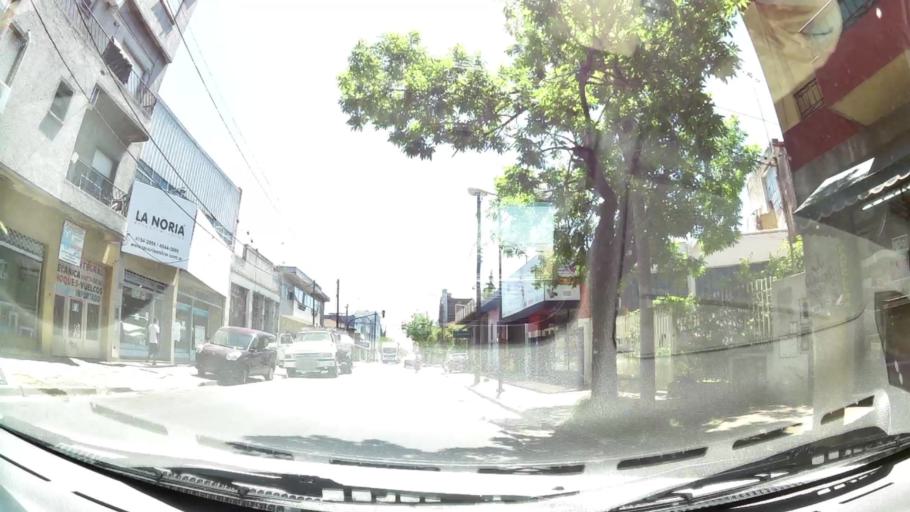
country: AR
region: Buenos Aires
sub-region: Partido de General San Martin
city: General San Martin
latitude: -34.5515
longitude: -58.5304
